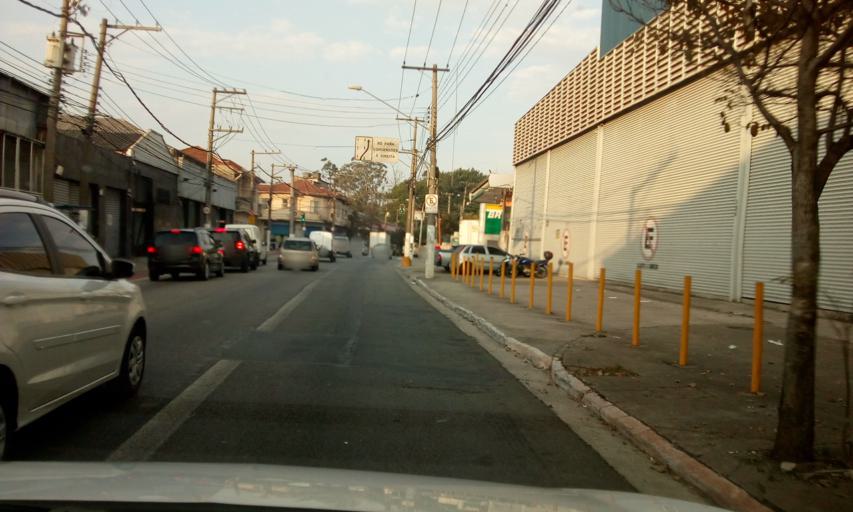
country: BR
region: Sao Paulo
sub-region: Sao Paulo
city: Sao Paulo
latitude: -23.5307
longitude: -46.6012
